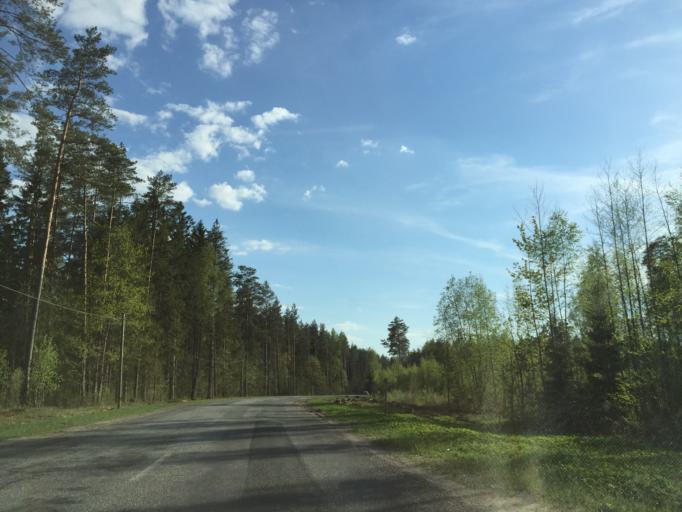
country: LV
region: Sigulda
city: Sigulda
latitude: 57.2442
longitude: 24.8649
